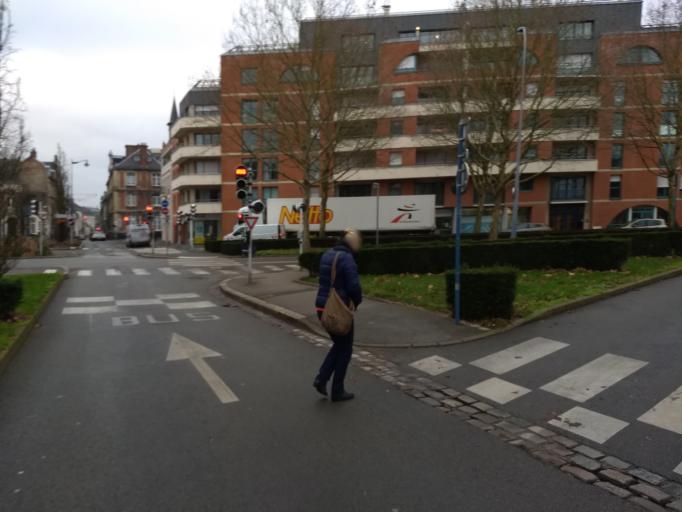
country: FR
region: Nord-Pas-de-Calais
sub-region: Departement du Pas-de-Calais
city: Arras
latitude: 50.2887
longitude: 2.7817
